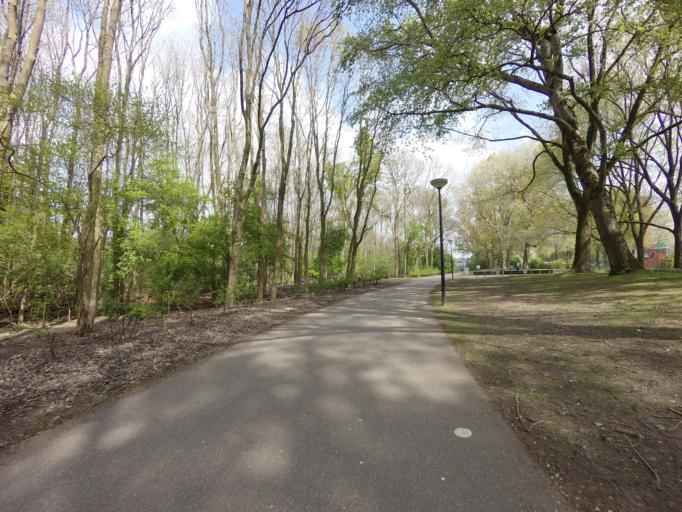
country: NL
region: North Holland
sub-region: Gemeente Zaanstad
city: Zaandam
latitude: 52.3680
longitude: 4.8150
